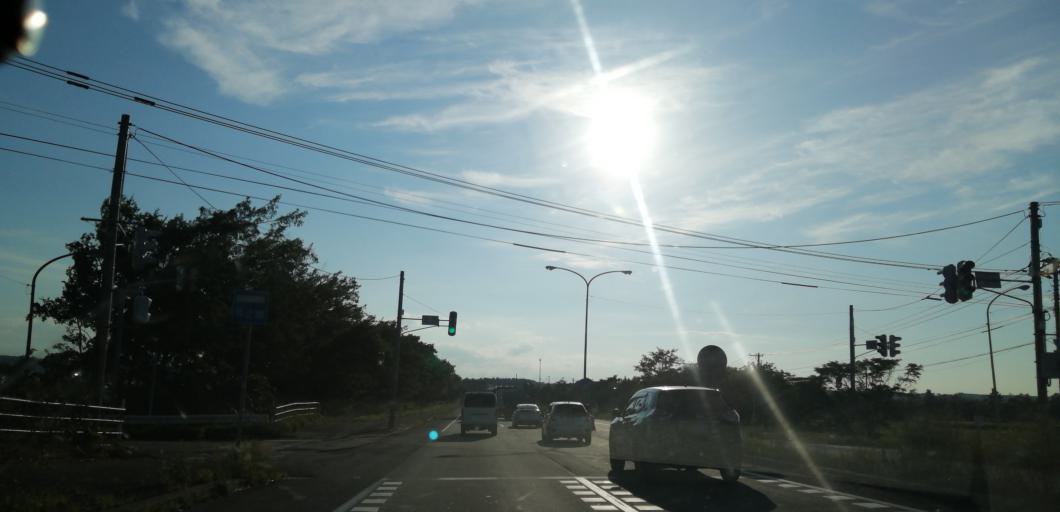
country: JP
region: Hokkaido
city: Kitahiroshima
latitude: 42.9973
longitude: 141.5770
